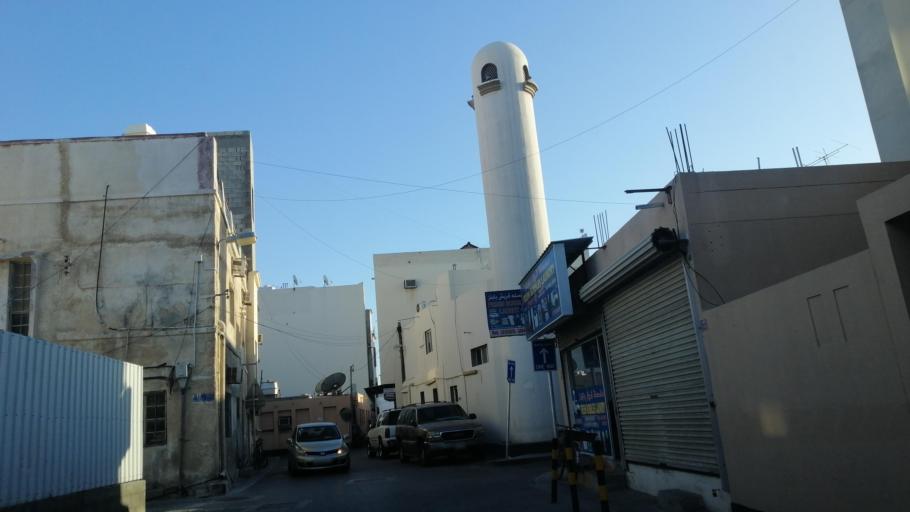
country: BH
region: Muharraq
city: Al Hadd
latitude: 26.2391
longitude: 50.6536
